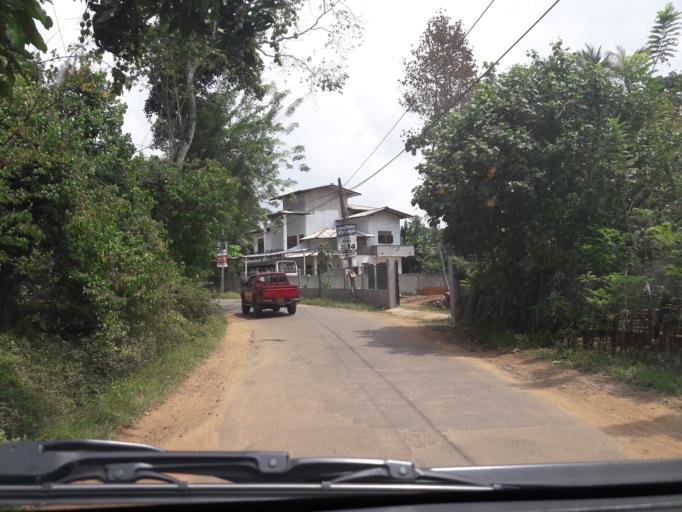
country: LK
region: Southern
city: Hikkaduwa
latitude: 6.0973
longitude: 80.1532
